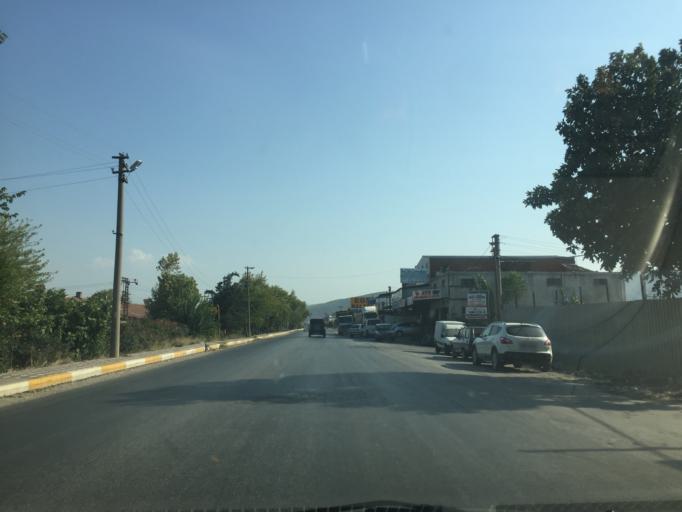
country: TR
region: Manisa
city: Akhisar
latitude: 38.9065
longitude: 27.8369
